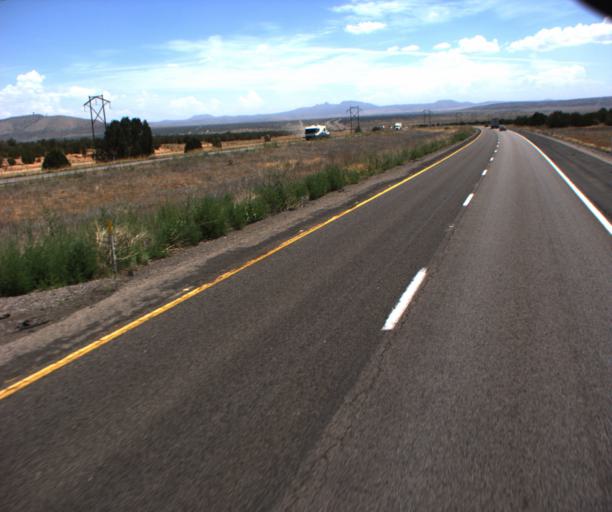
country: US
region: Arizona
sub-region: Mohave County
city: Peach Springs
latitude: 35.3023
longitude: -113.0064
